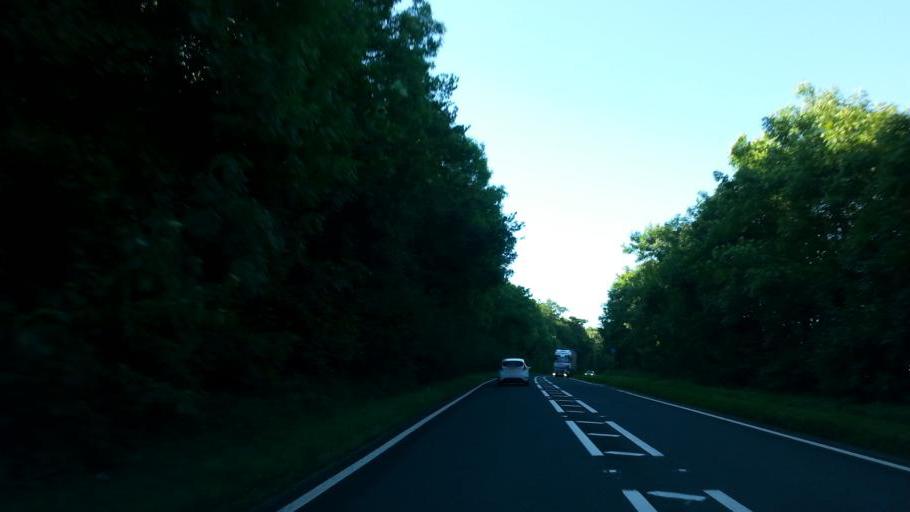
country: GB
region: England
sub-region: Lincolnshire
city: Stamford
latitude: 52.6340
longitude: -0.4933
